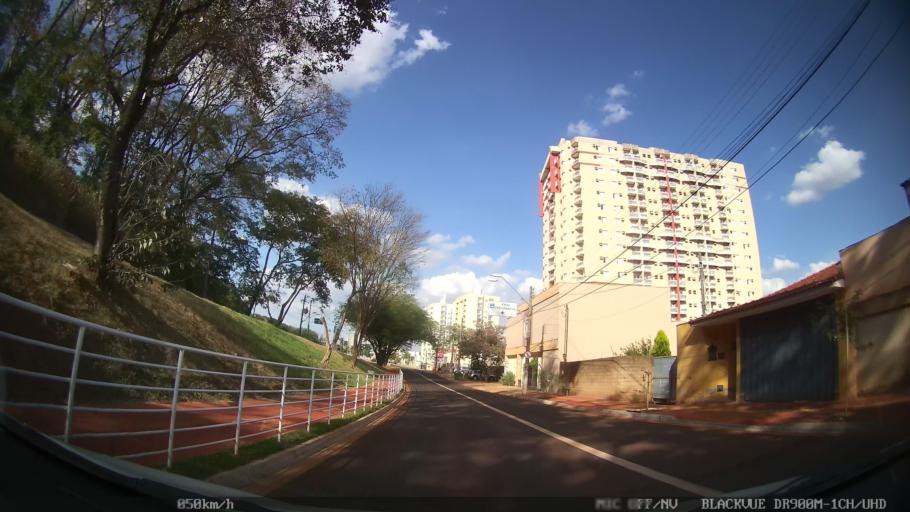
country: BR
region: Sao Paulo
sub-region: Ribeirao Preto
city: Ribeirao Preto
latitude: -21.1743
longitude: -47.8407
